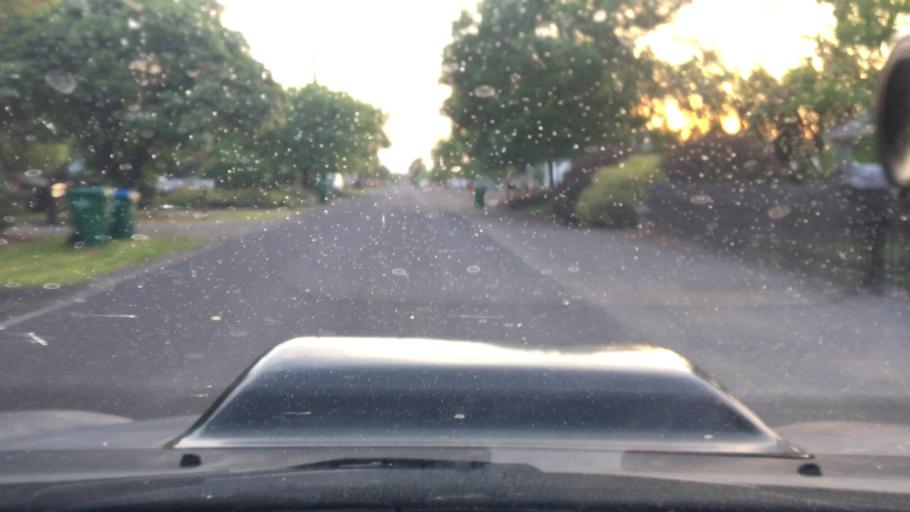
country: US
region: California
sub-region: Butte County
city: Chico
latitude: 39.7078
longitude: -121.8413
